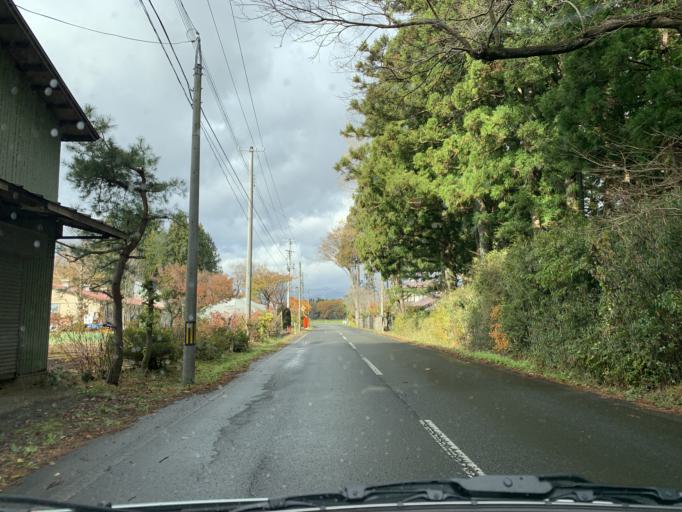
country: JP
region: Iwate
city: Mizusawa
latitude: 39.0897
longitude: 141.0180
